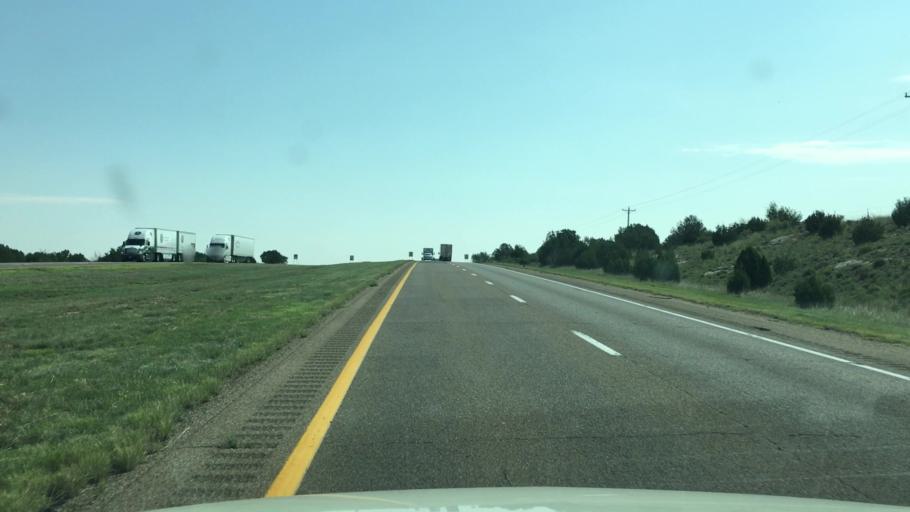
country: US
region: New Mexico
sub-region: Guadalupe County
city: Santa Rosa
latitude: 35.0205
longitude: -104.4336
